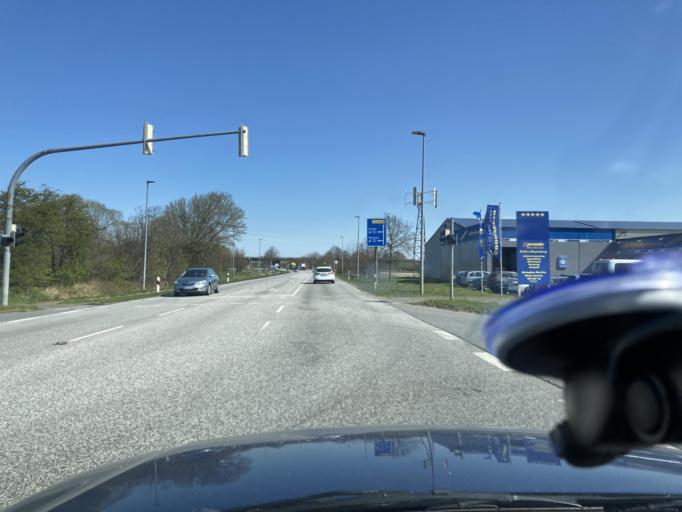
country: DE
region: Schleswig-Holstein
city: Hemmingstedt
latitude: 54.1650
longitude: 9.0882
